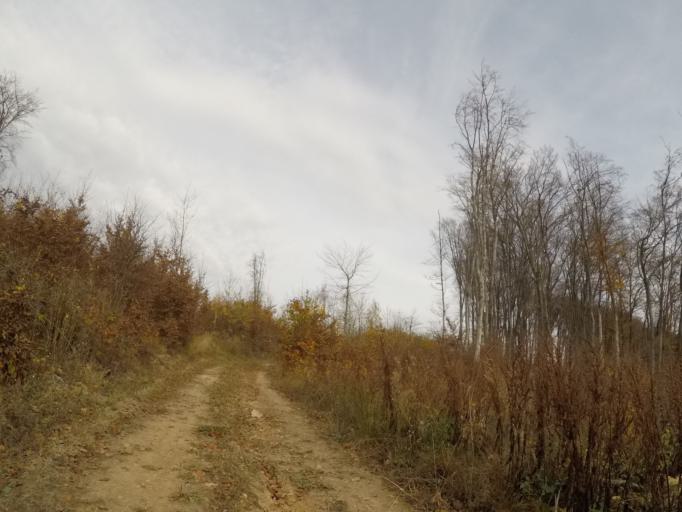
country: SK
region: Presovsky
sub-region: Okres Presov
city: Presov
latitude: 48.9572
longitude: 21.2100
